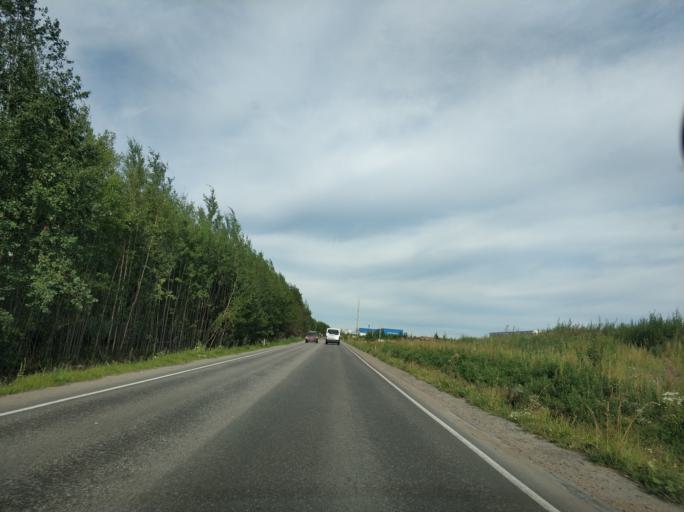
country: RU
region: St.-Petersburg
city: Grazhdanka
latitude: 60.0460
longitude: 30.4200
